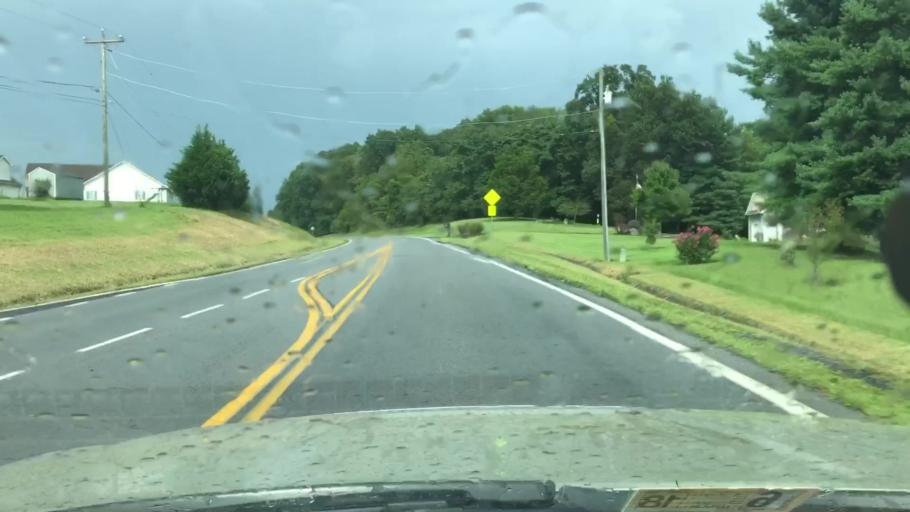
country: US
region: Virginia
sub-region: City of Waynesboro
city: Waynesboro
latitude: 38.0908
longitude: -78.8999
